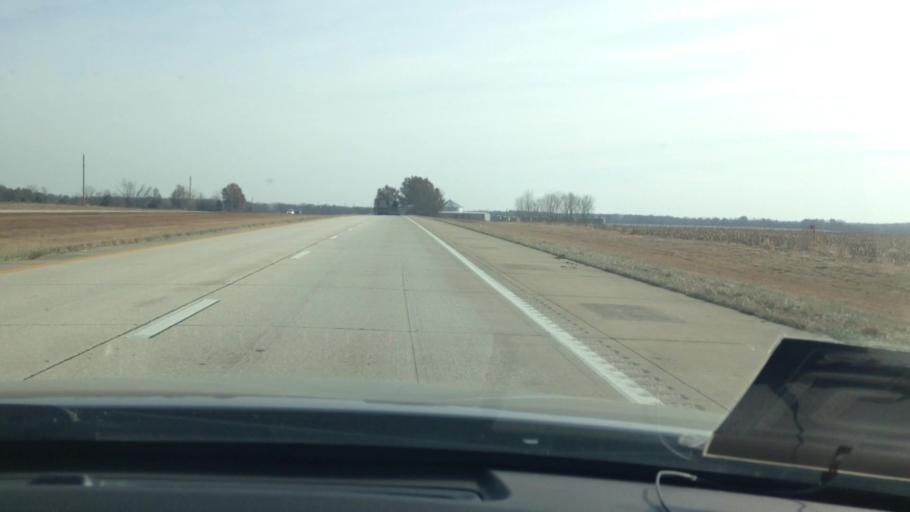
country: US
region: Missouri
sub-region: Henry County
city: Clinton
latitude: 38.4312
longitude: -93.9268
